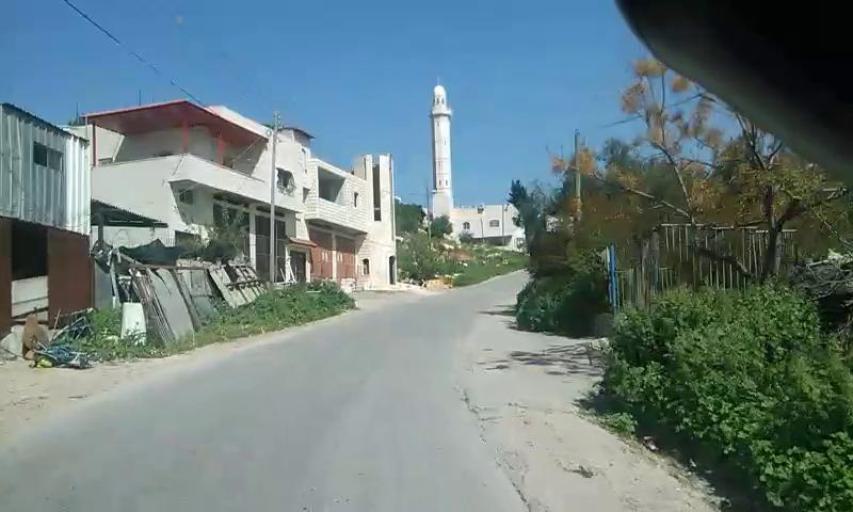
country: PS
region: West Bank
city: Idhna
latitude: 31.5540
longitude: 34.9718
